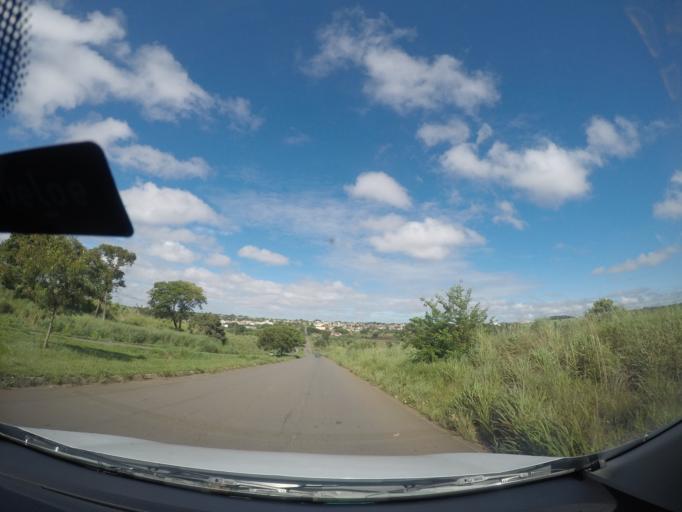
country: BR
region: Goias
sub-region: Senador Canedo
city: Senador Canedo
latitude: -16.6504
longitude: -49.1634
